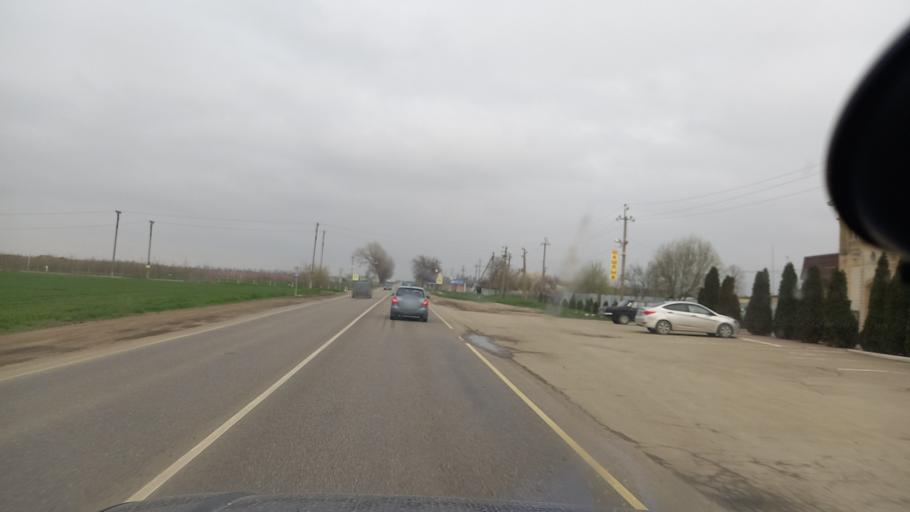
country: RU
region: Krasnodarskiy
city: Slavyansk-na-Kubani
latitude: 45.2430
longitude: 38.0369
